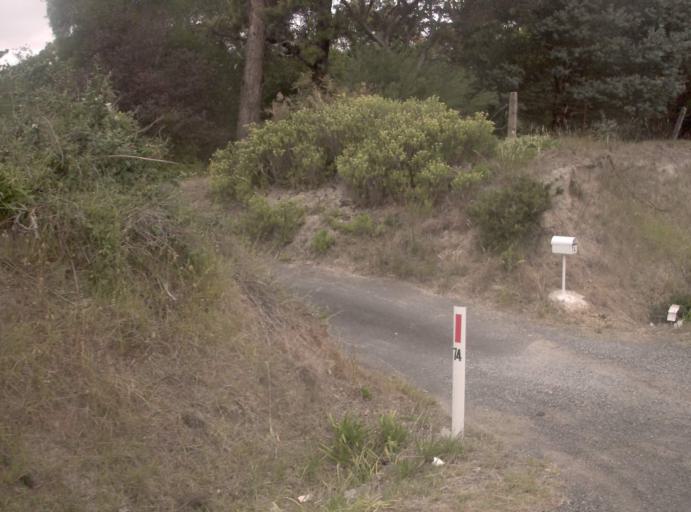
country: AU
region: Victoria
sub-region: Casey
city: Endeavour Hills
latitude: -37.9787
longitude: 145.2787
